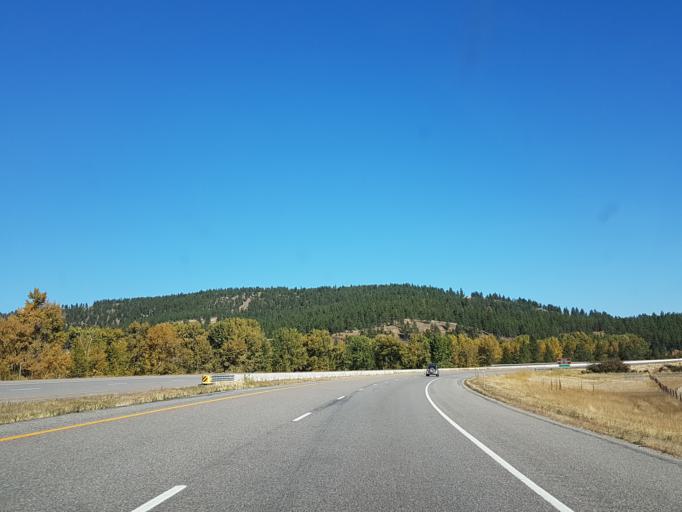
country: US
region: Montana
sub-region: Missoula County
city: Frenchtown
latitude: 47.0230
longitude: -114.3916
